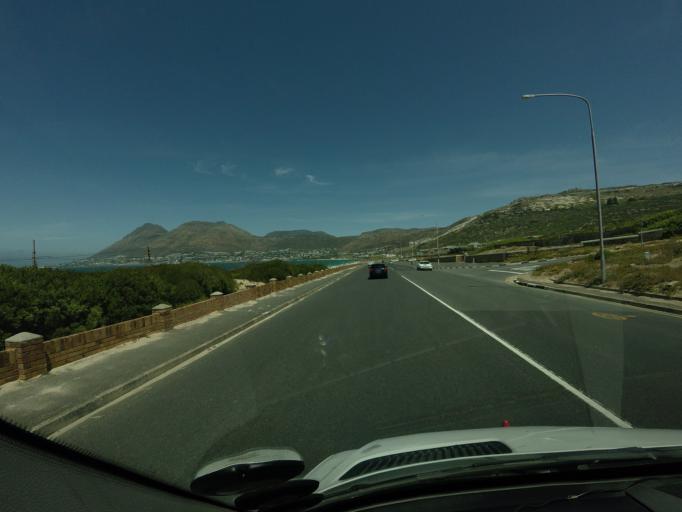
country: ZA
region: Western Cape
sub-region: City of Cape Town
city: Retreat
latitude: -34.1658
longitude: 18.4312
